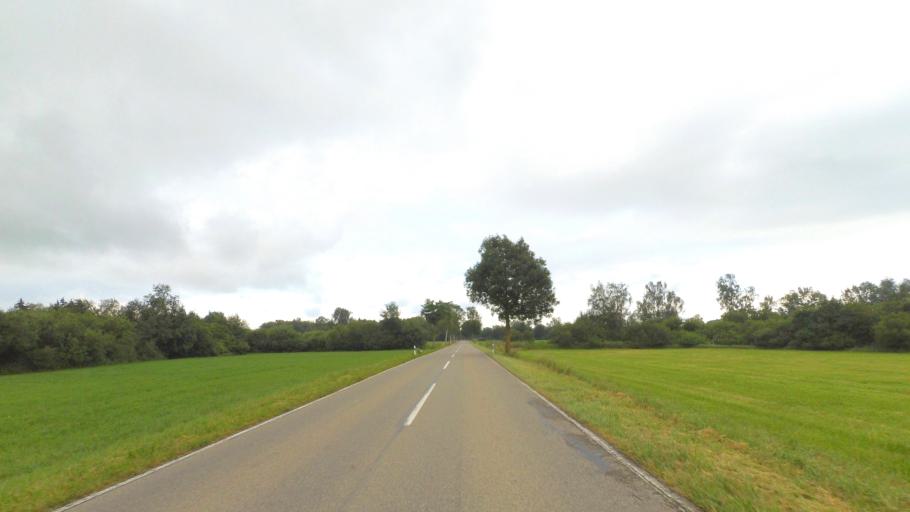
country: DE
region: Baden-Wuerttemberg
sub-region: Tuebingen Region
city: Langenau
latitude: 48.4725
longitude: 10.1566
